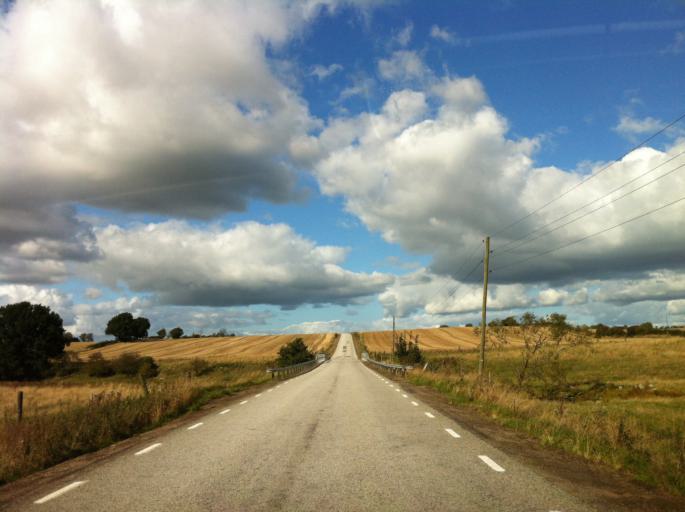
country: SE
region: Skane
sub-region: Sjobo Kommun
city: Sjoebo
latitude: 55.6423
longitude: 13.8206
